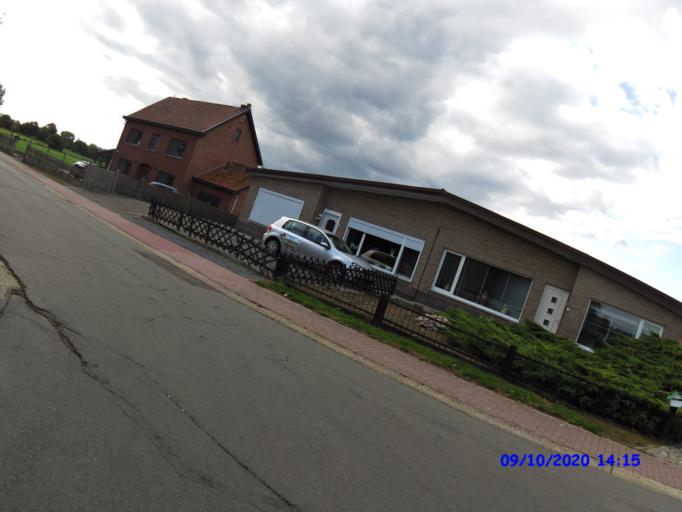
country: BE
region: Flanders
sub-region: Provincie Limburg
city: Nieuwerkerken
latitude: 50.8393
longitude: 5.2264
